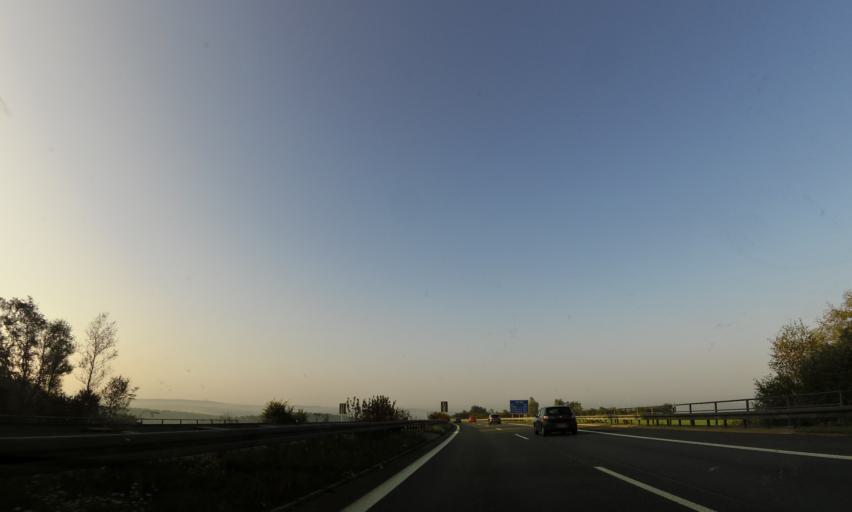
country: DE
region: Saxony
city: Reichenbach/Vogtland
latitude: 50.5918
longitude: 12.3292
